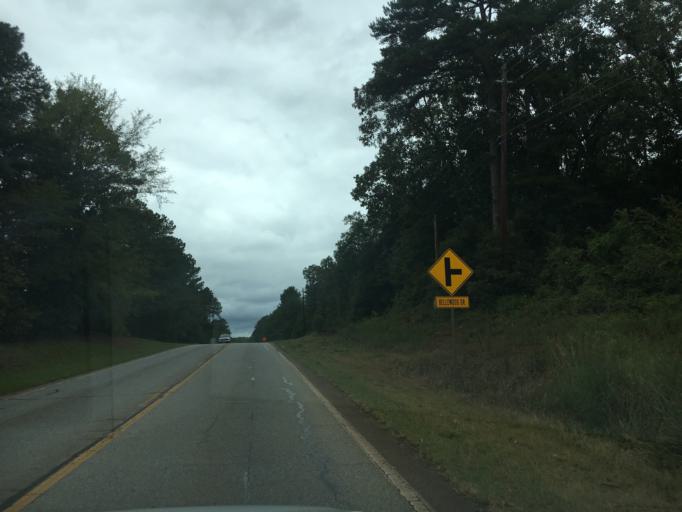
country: US
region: Georgia
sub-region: Wilkes County
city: Washington
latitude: 33.6897
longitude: -82.6642
